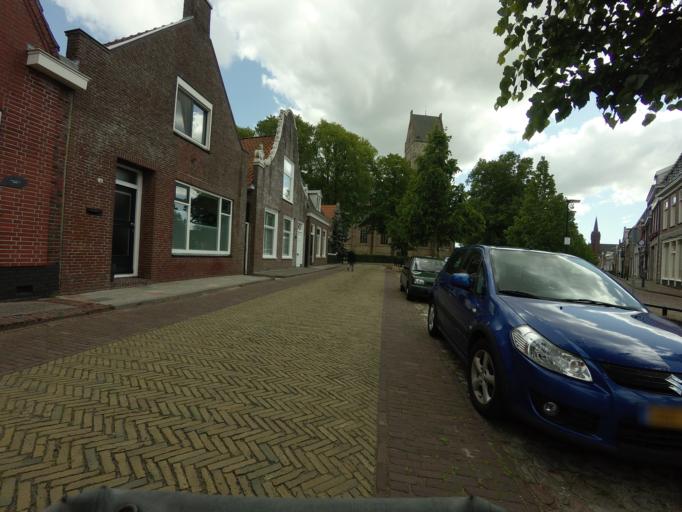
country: NL
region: Friesland
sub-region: Sudwest Fryslan
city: Bolsward
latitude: 53.0656
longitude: 5.5264
